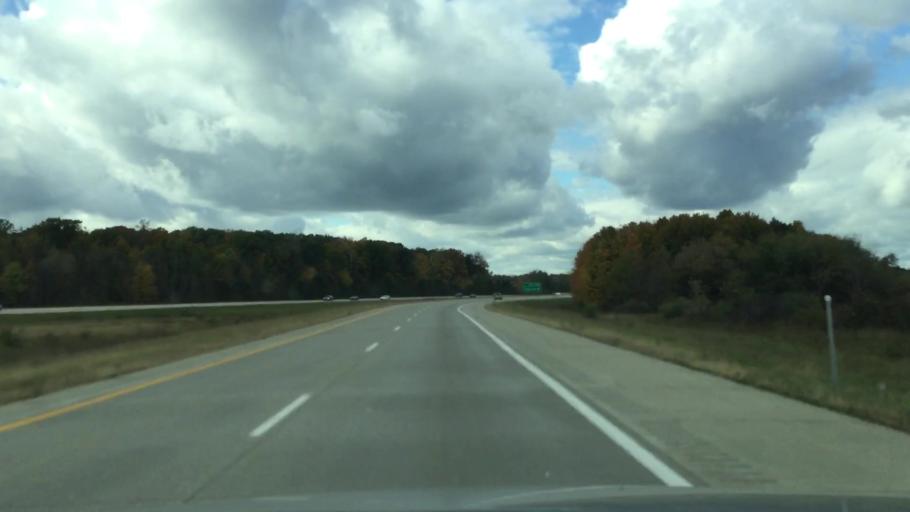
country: US
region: Michigan
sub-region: Genesee County
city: Davison
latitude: 43.0168
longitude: -83.4273
